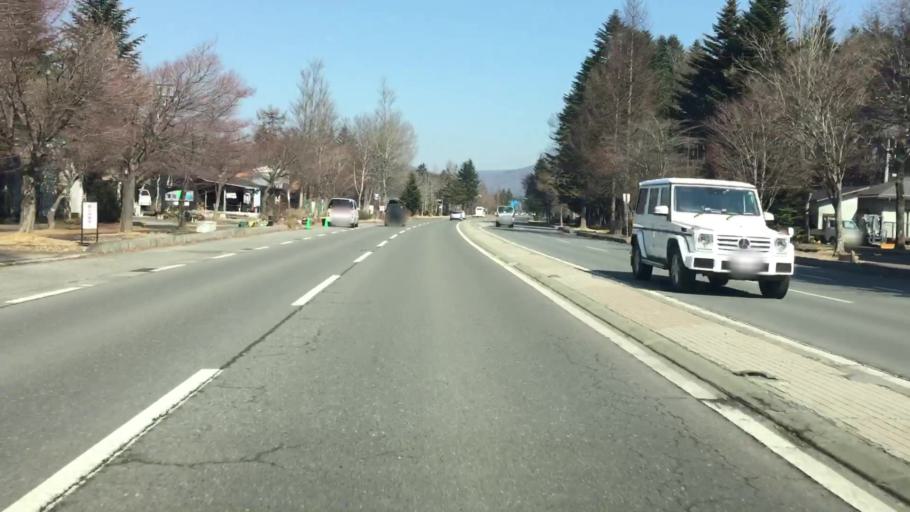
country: JP
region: Nagano
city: Saku
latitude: 36.3341
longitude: 138.6314
